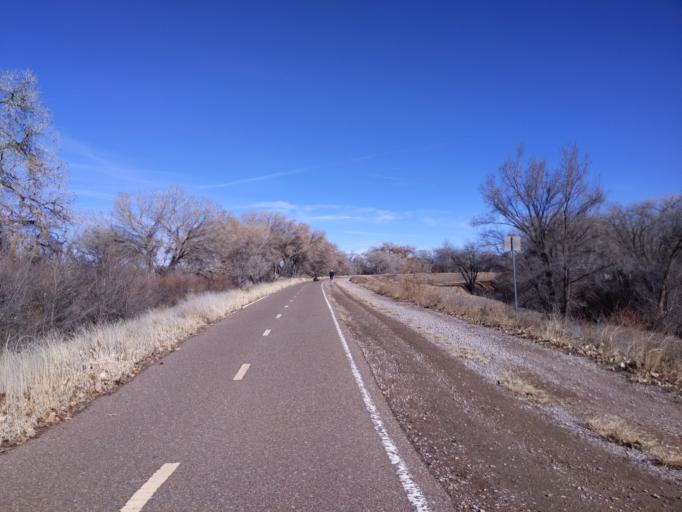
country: US
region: New Mexico
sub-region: Bernalillo County
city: Lee Acres
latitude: 35.1594
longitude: -106.6667
